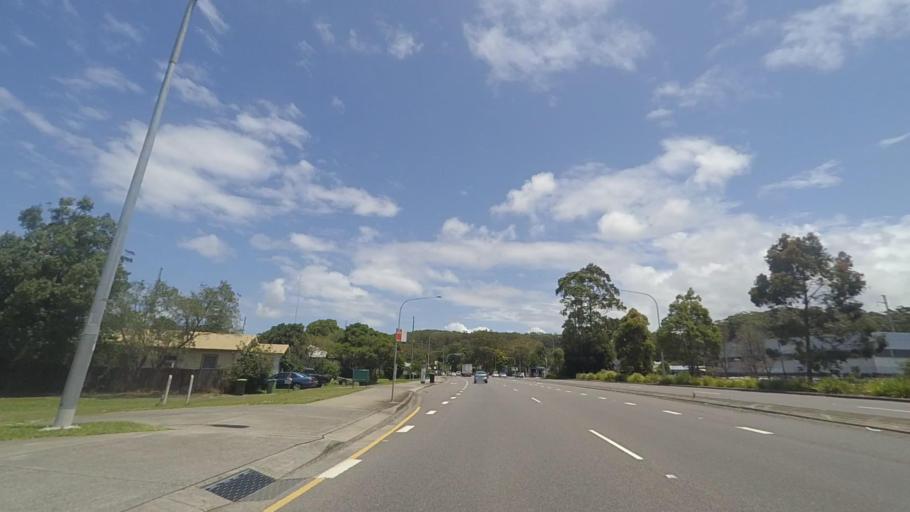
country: AU
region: New South Wales
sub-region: Gosford Shire
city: Lisarow
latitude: -33.3480
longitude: 151.3701
